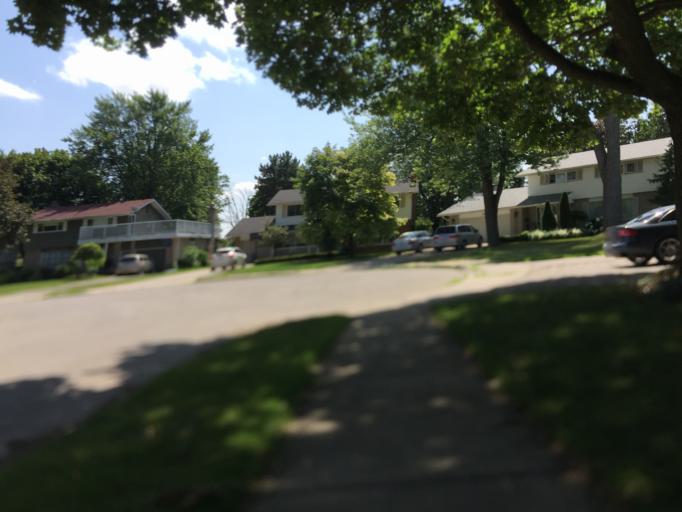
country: CA
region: Ontario
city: Stratford
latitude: 43.3799
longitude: -80.9956
